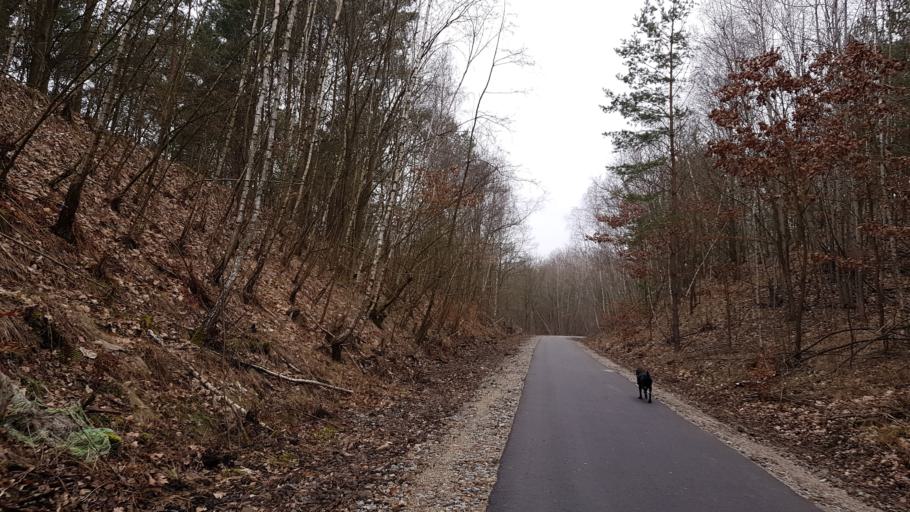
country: PL
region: West Pomeranian Voivodeship
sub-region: Powiat mysliborski
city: Barlinek
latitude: 53.0088
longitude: 15.2417
